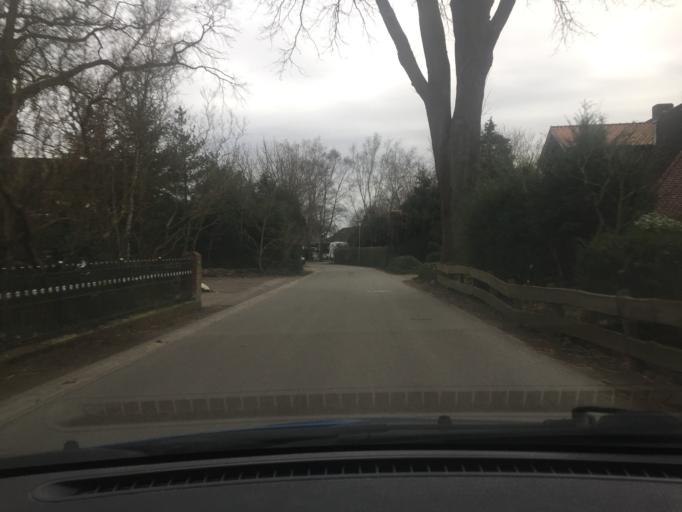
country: DE
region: Lower Saxony
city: Salzhausen
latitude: 53.2259
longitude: 10.1931
